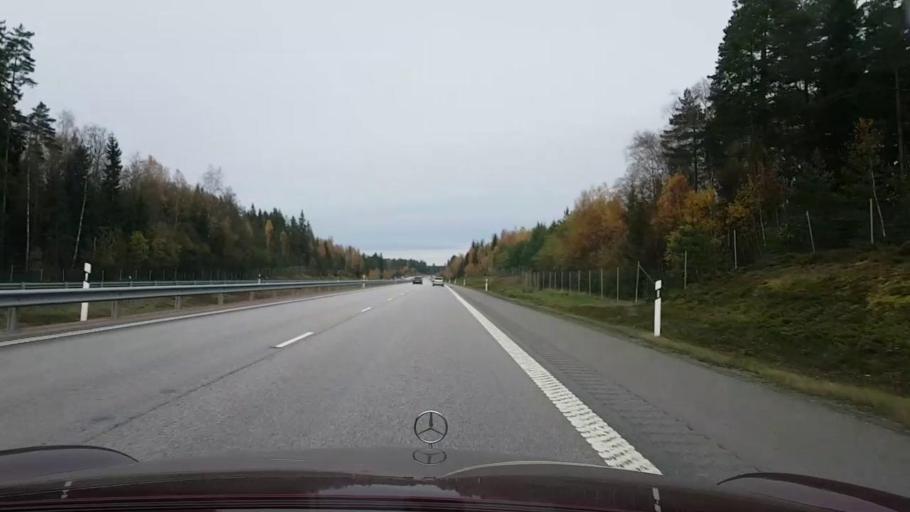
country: SE
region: OErebro
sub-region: Lindesbergs Kommun
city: Fellingsbro
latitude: 59.3568
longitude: 15.5657
